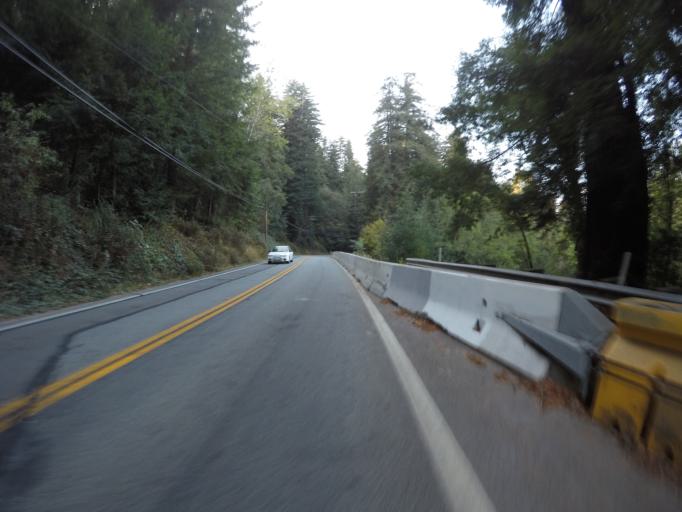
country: US
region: California
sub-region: Santa Cruz County
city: Pasatiempo
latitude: 36.9962
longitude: -122.0366
